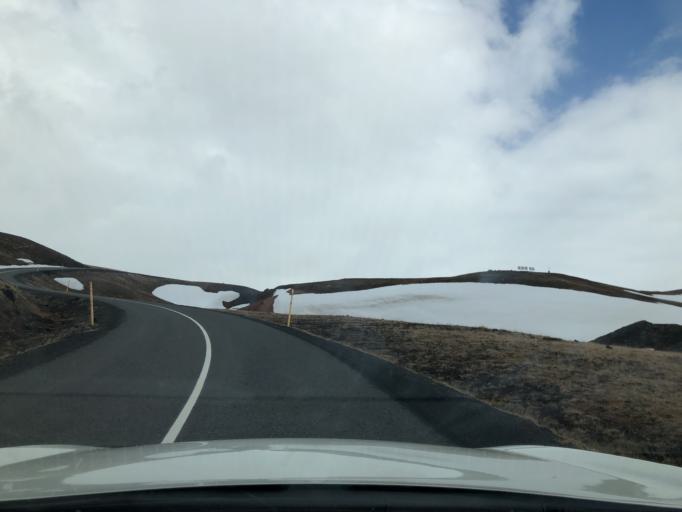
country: IS
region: Northeast
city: Laugar
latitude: 65.7089
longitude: -16.7711
